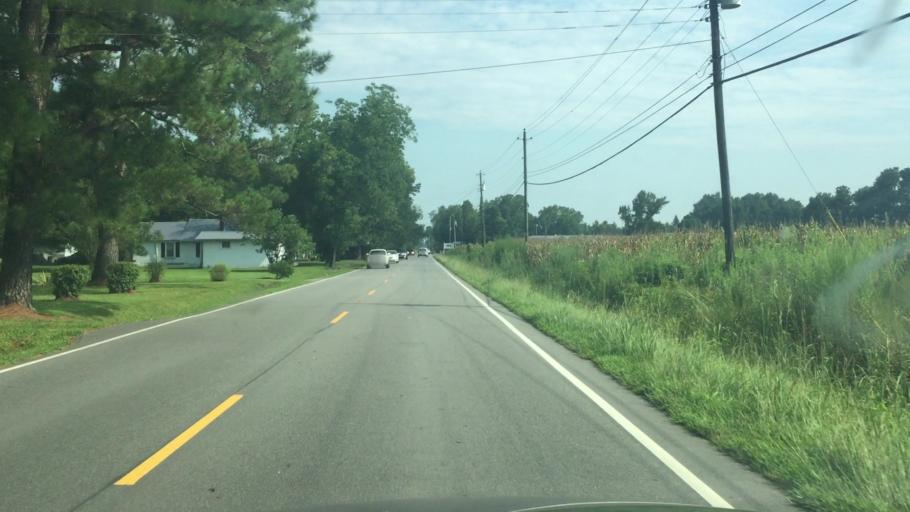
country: US
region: North Carolina
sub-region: Columbus County
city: Chadbourn
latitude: 34.3081
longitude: -78.8264
